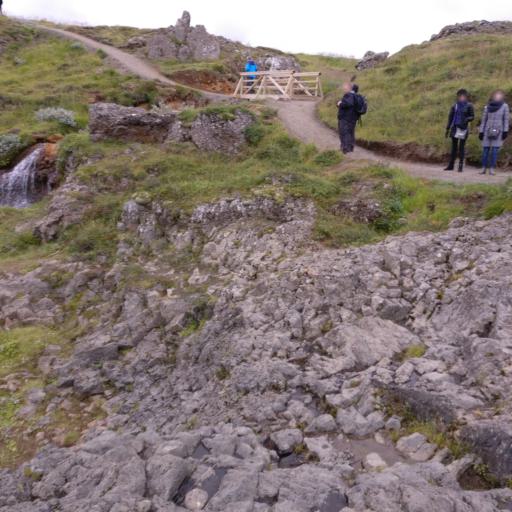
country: IS
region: Northeast
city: Laugar
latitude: 65.6849
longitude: -17.5417
